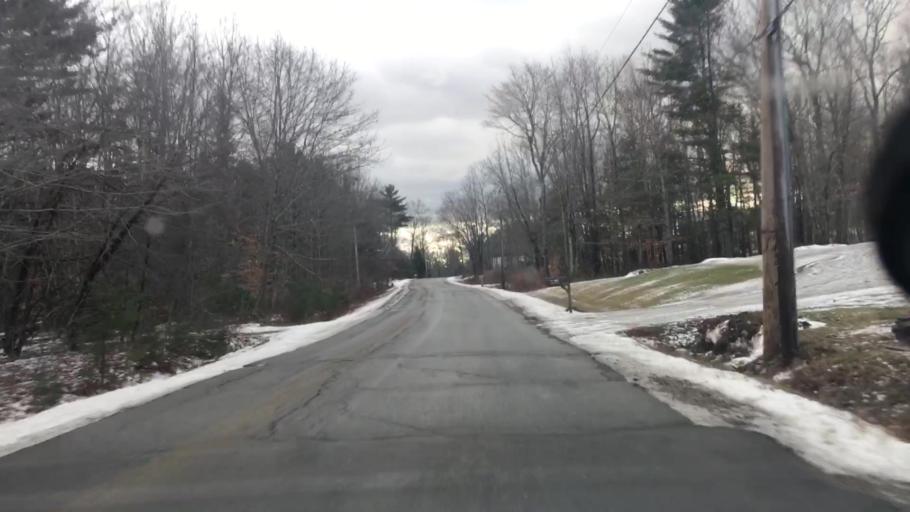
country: US
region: Maine
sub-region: Hancock County
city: Dedham
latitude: 44.6399
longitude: -68.7045
